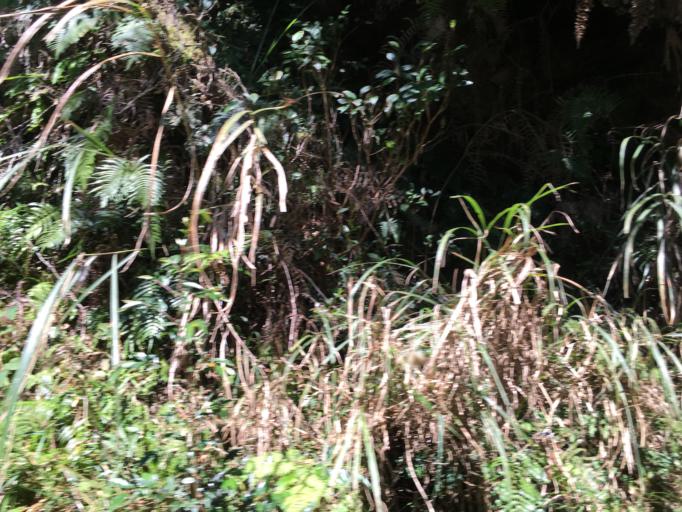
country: TW
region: Taiwan
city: Daxi
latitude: 24.5301
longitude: 121.4017
